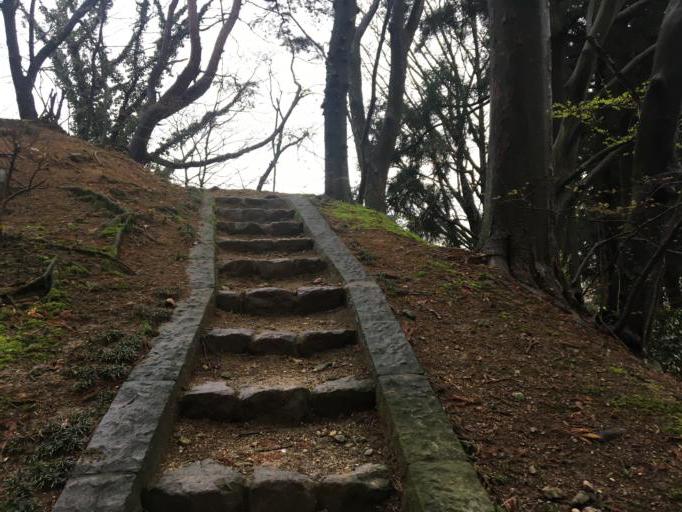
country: JP
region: Akita
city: Akita
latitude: 39.7230
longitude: 140.1241
